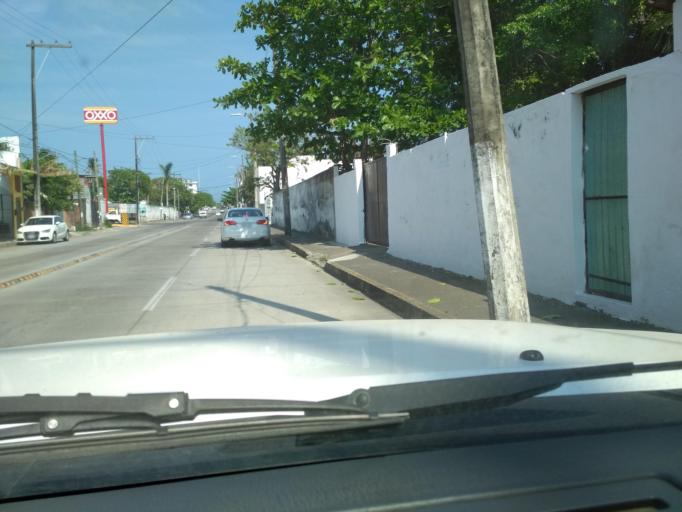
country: MX
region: Veracruz
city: Boca del Rio
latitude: 19.1000
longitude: -96.1103
